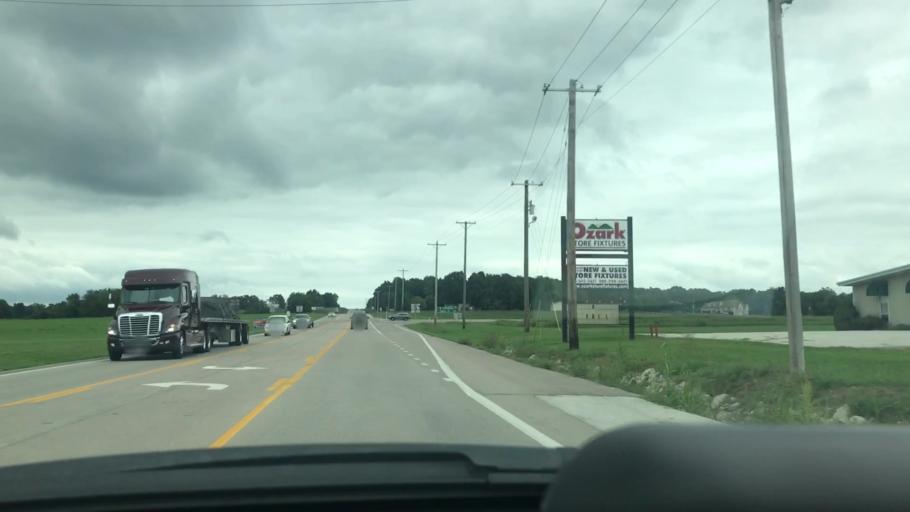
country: US
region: Missouri
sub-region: Dallas County
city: Buffalo
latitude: 37.6660
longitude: -93.1034
